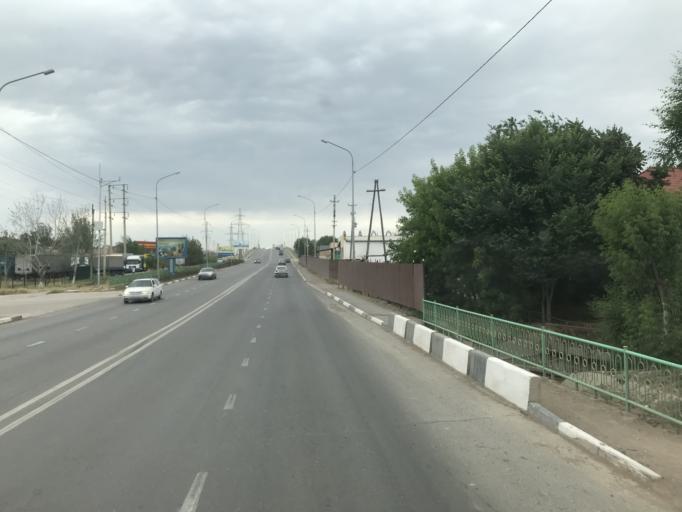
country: KZ
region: Ongtustik Qazaqstan
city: Saryaghash
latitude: 41.4619
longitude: 69.1526
